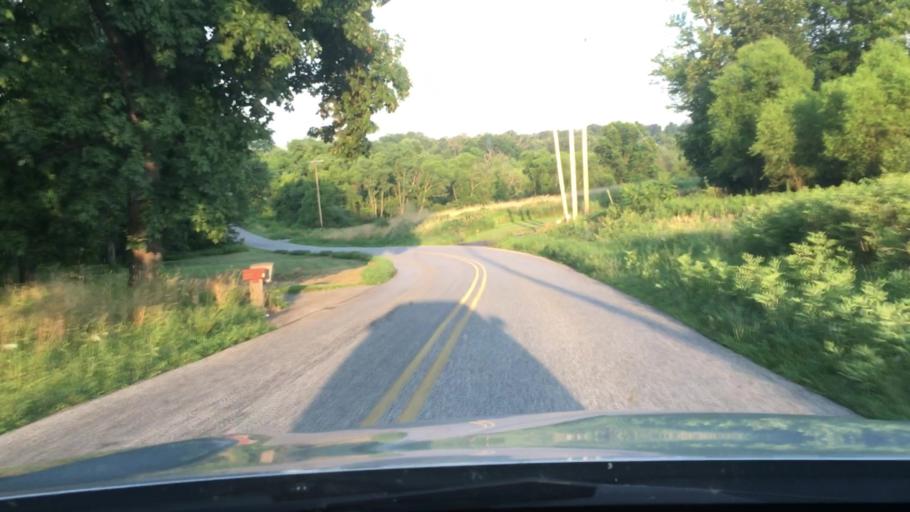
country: US
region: Pennsylvania
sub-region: York County
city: Dover
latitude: 40.0265
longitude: -76.8427
